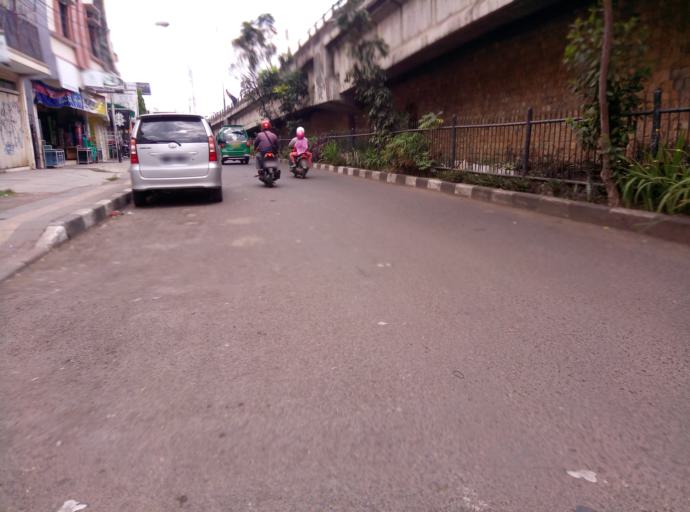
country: ID
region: West Java
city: Bandung
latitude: -6.9275
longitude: 107.6445
